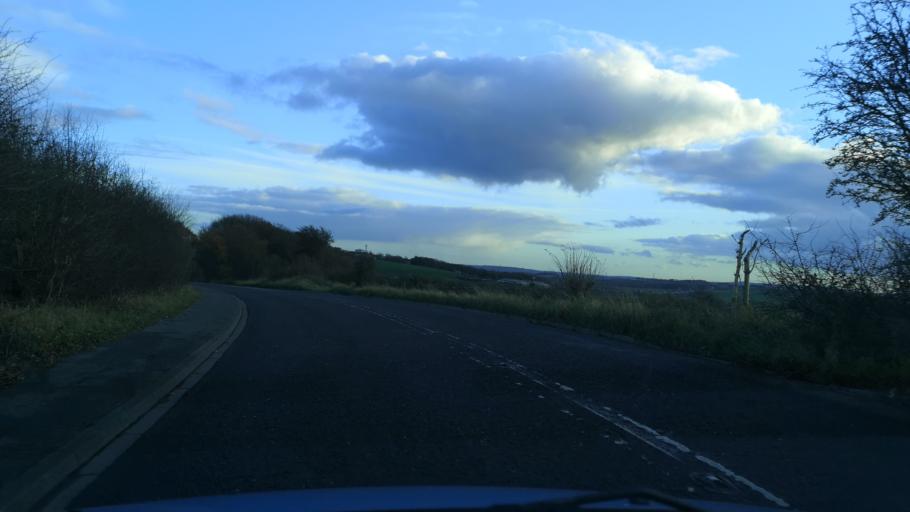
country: GB
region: England
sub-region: City and Borough of Wakefield
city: Ossett
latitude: 53.7112
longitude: -1.5694
